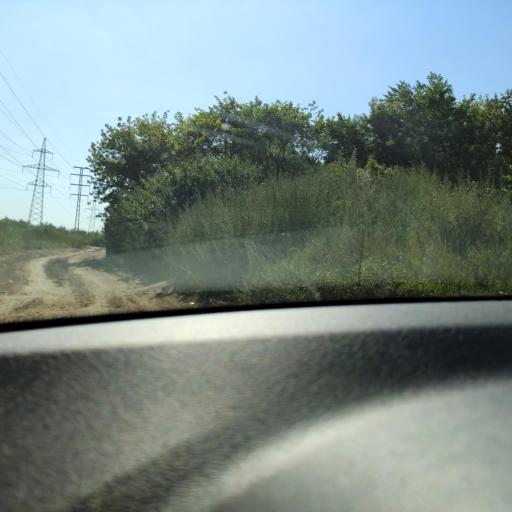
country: RU
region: Samara
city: Samara
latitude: 53.1748
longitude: 50.2125
